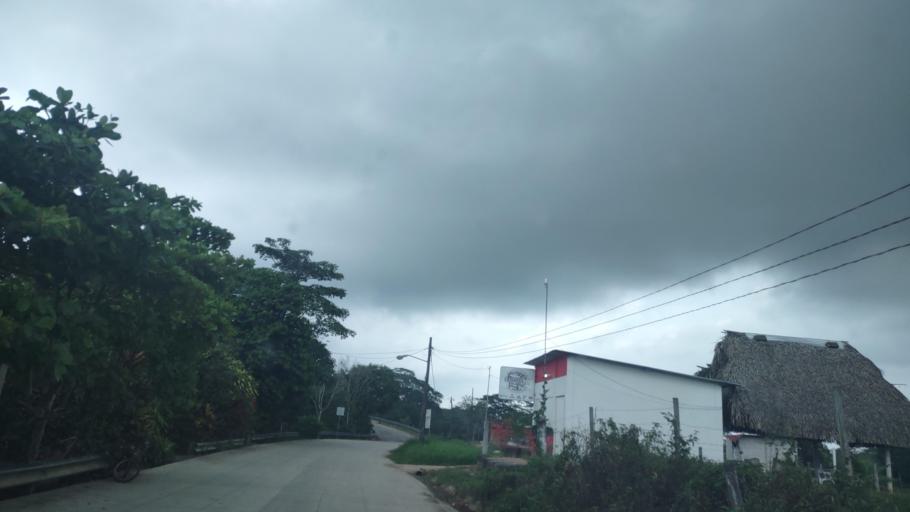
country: MX
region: Veracruz
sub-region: Uxpanapa
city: Poblado 10
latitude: 17.4945
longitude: -94.1654
